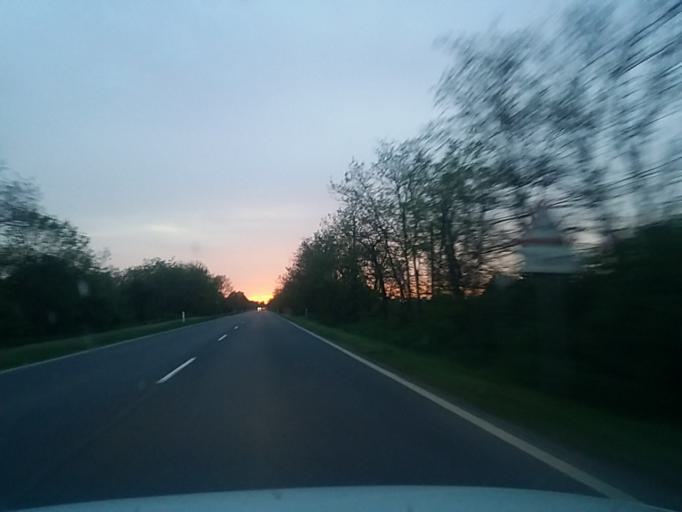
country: HU
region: Bekes
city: Kondoros
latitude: 46.7478
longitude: 20.8475
